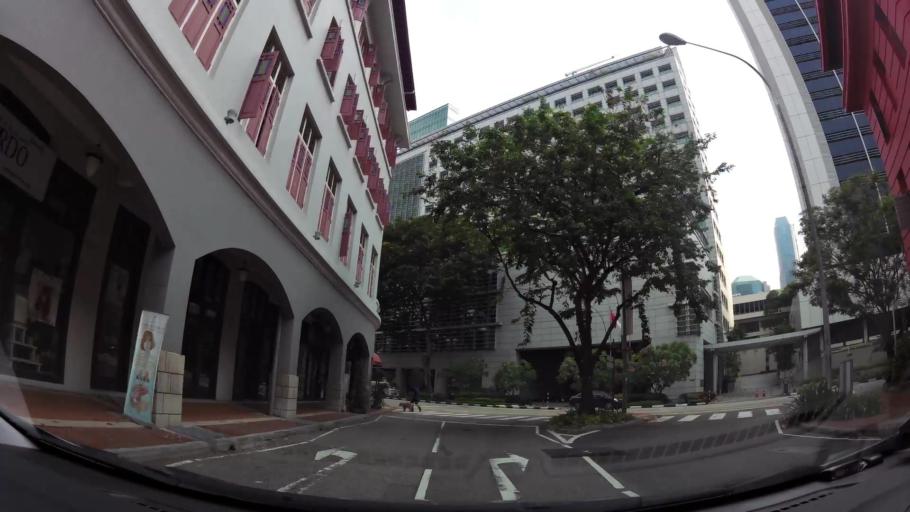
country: SG
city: Singapore
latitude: 1.2788
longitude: 103.8449
